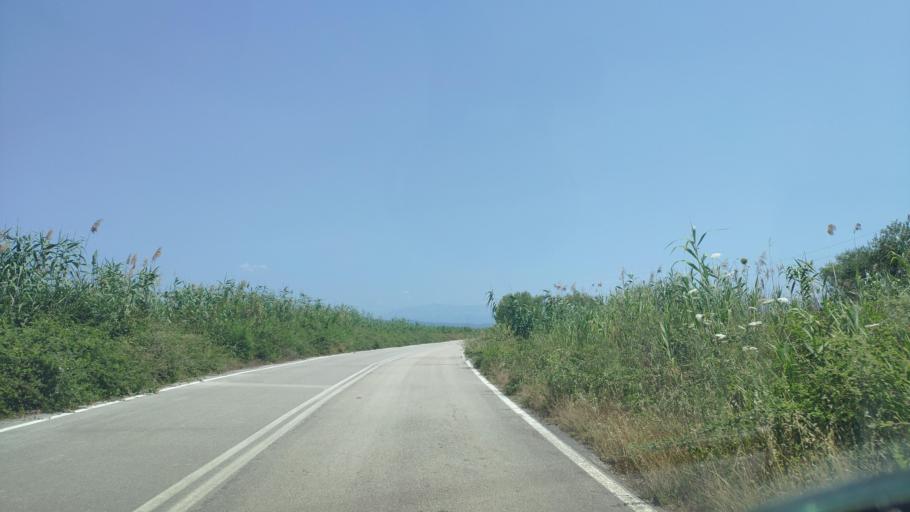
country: GR
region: Epirus
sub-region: Nomos Artas
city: Aneza
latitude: 39.0568
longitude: 20.8655
